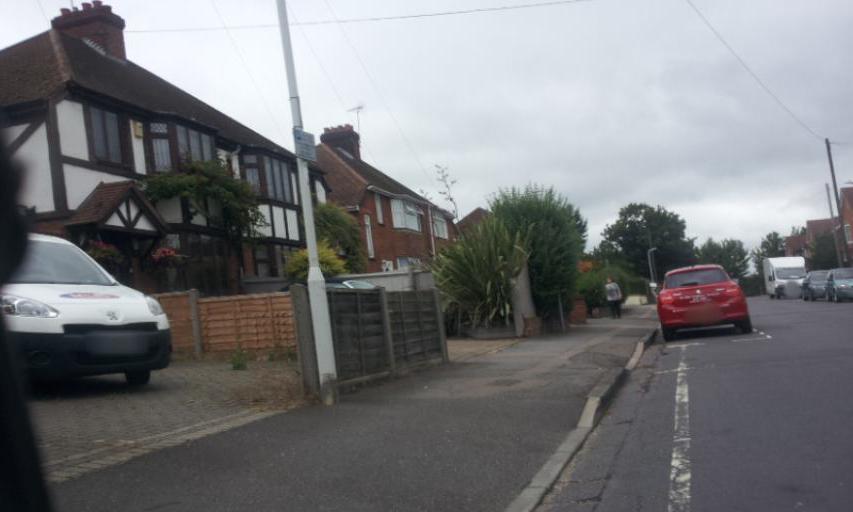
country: GB
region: England
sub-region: Kent
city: Sittingbourne
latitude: 51.3424
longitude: 0.7282
